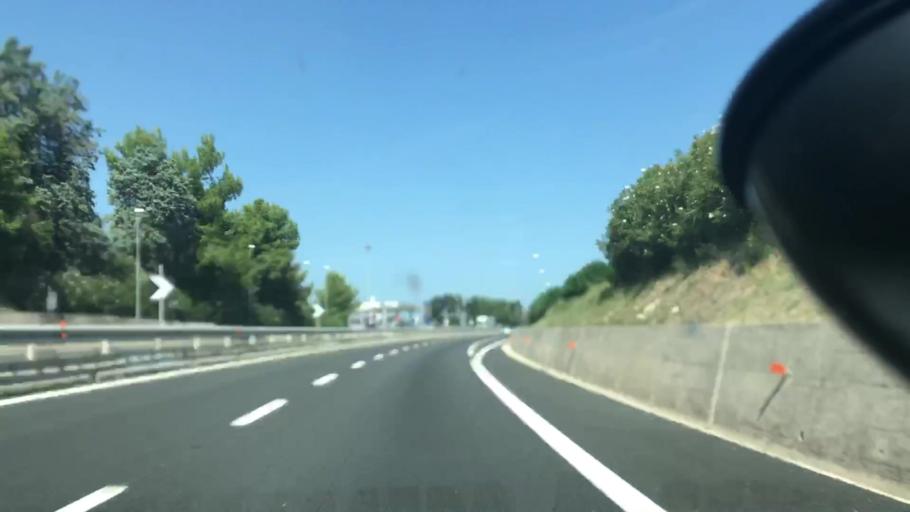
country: IT
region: Abruzzo
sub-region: Provincia di Chieti
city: Miglianico
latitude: 42.3846
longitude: 14.2891
